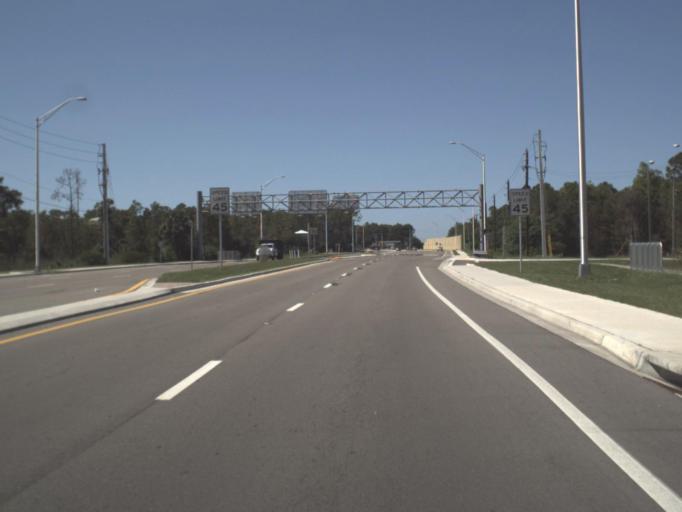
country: US
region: Florida
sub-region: Collier County
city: Golden Gate
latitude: 26.1549
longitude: -81.6892
